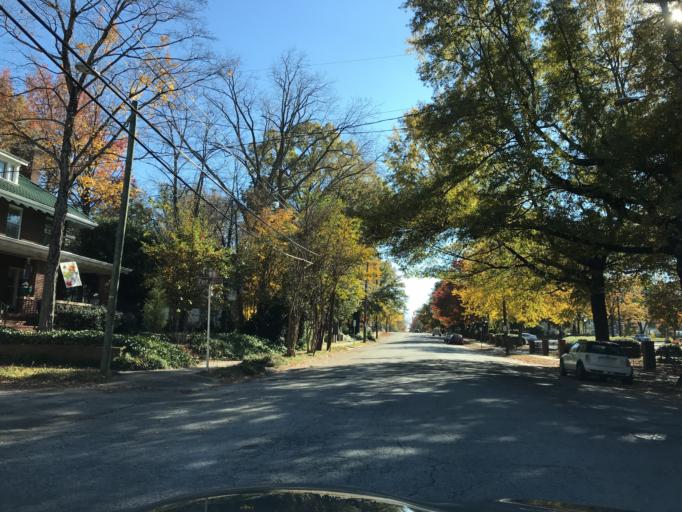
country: US
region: North Carolina
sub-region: Wake County
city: Raleigh
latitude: 35.7893
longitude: -78.6360
